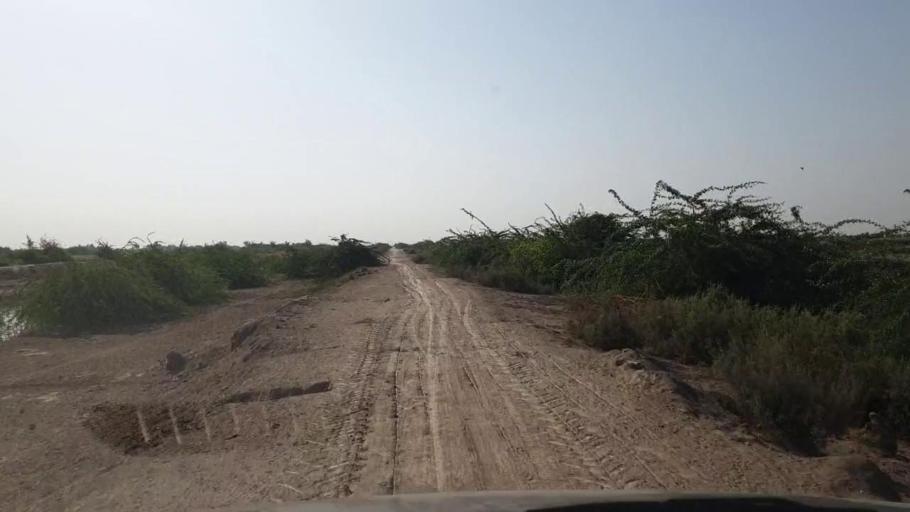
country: PK
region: Sindh
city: Kadhan
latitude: 24.5823
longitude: 69.0792
